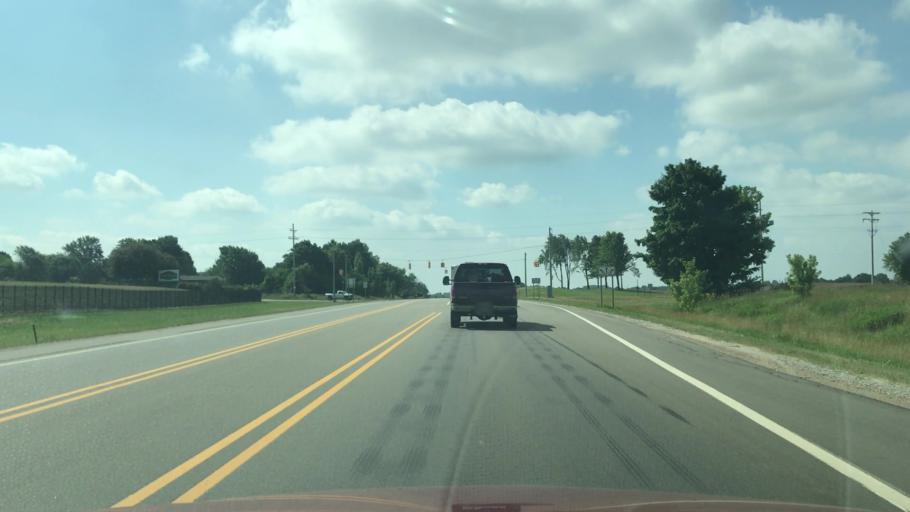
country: US
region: Michigan
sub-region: Kent County
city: Sparta
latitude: 43.1478
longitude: -85.7225
